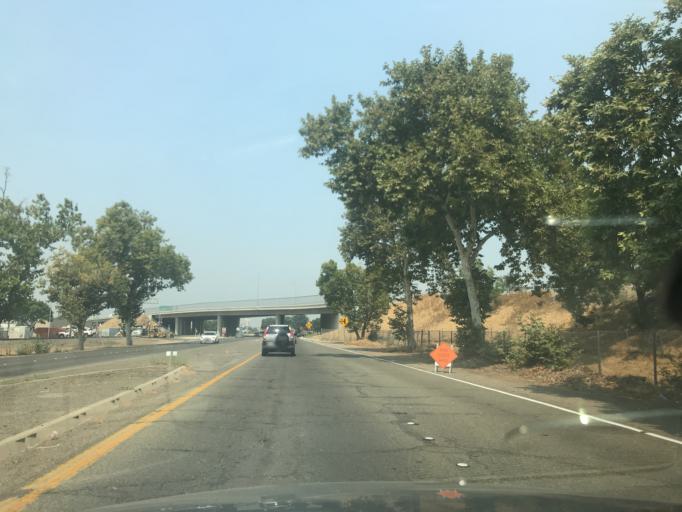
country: US
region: California
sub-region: Merced County
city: Merced
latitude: 37.2948
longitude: -120.4698
